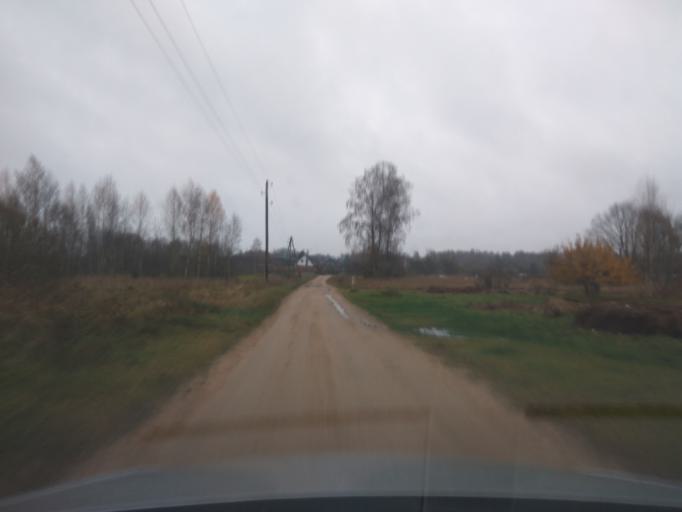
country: LV
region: Kuldigas Rajons
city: Kuldiga
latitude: 56.9258
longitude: 21.9667
